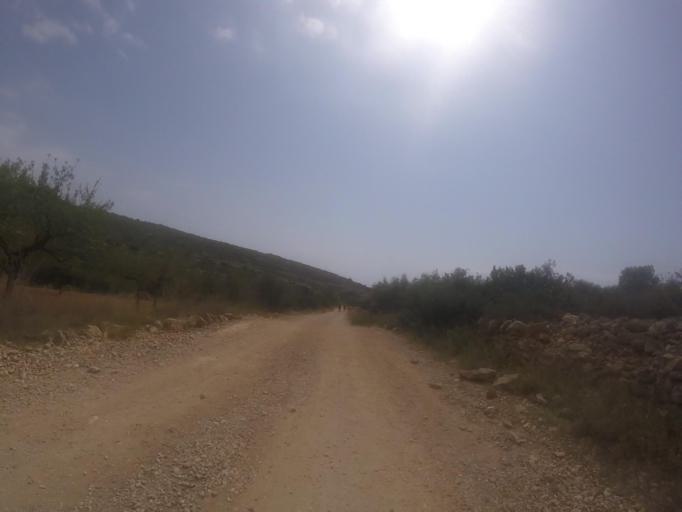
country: ES
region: Valencia
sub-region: Provincia de Castello
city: Peniscola
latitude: 40.3482
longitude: 0.3696
